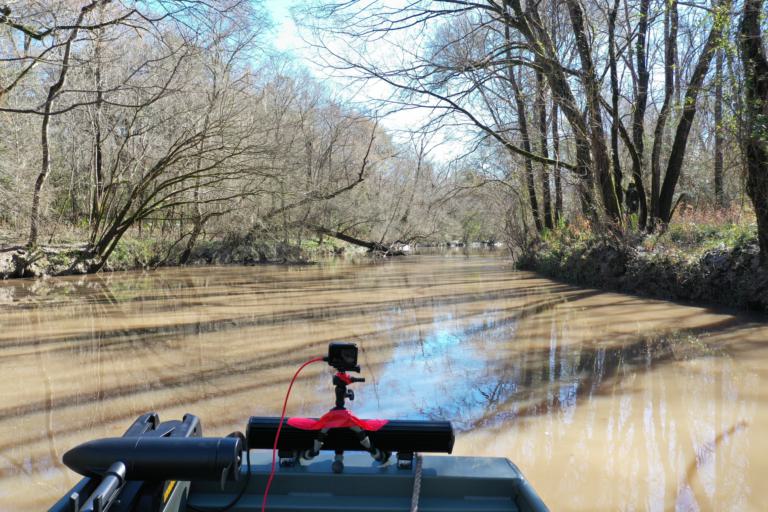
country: US
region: Louisiana
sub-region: Calcasieu Parish
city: Iowa
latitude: 30.3184
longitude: -93.0516
